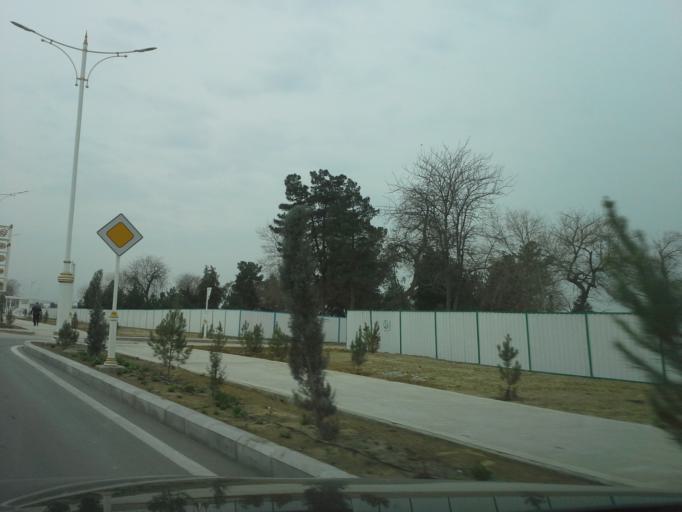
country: TM
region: Ahal
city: Ashgabat
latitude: 37.9584
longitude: 58.3430
